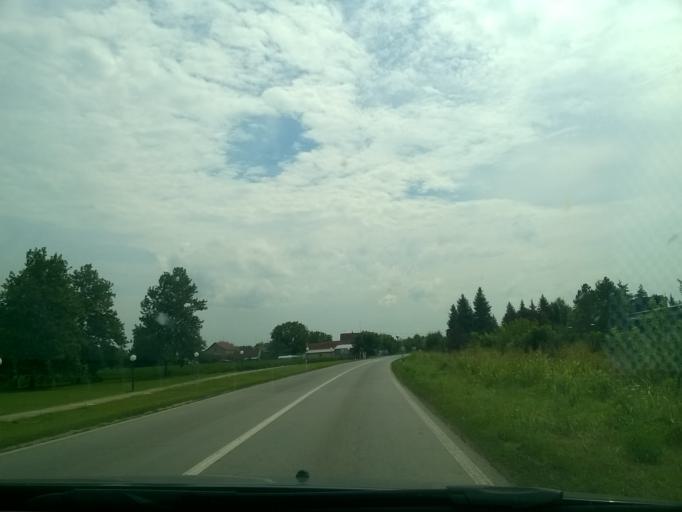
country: RS
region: Autonomna Pokrajina Vojvodina
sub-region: Juznobanatski Okrug
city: Plandiste
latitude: 45.2360
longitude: 21.1164
